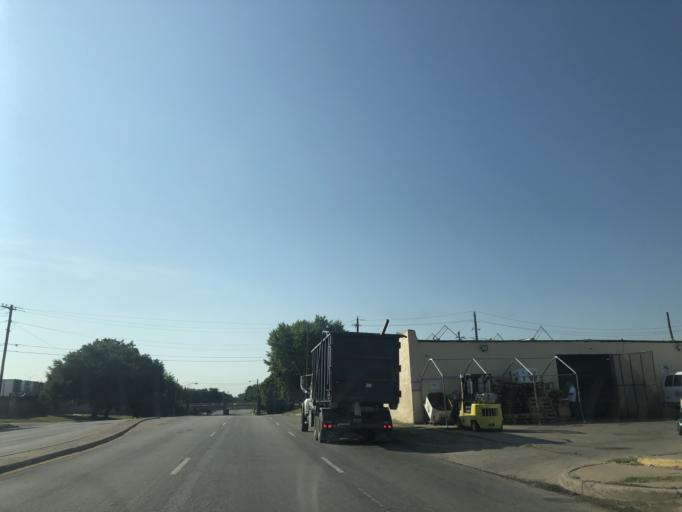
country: US
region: Texas
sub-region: Dallas County
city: Dallas
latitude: 32.7717
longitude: -96.7817
